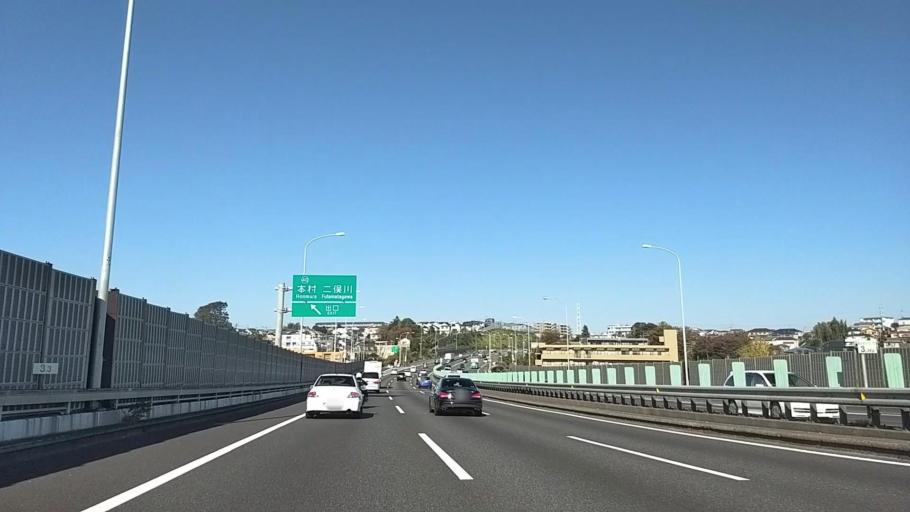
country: JP
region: Kanagawa
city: Minami-rinkan
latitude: 35.4656
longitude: 139.5372
